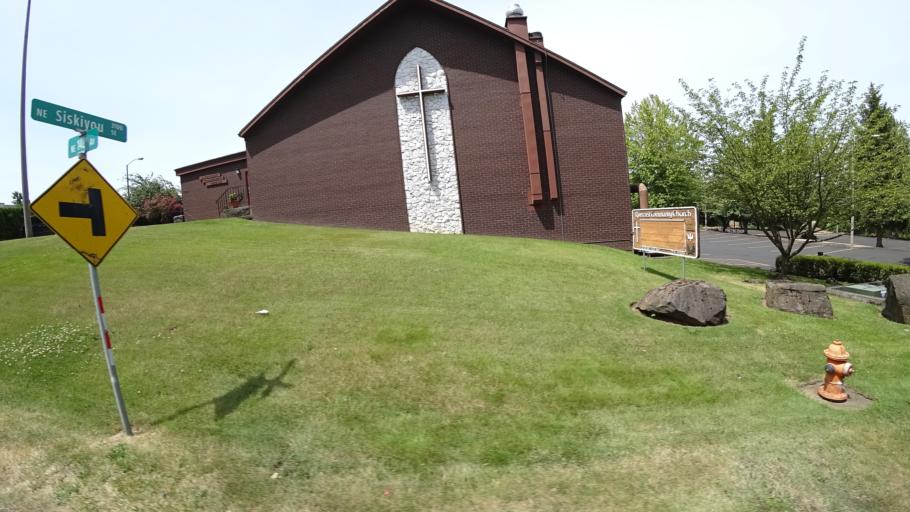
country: US
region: Oregon
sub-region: Multnomah County
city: Fairview
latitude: 45.5464
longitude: -122.5102
